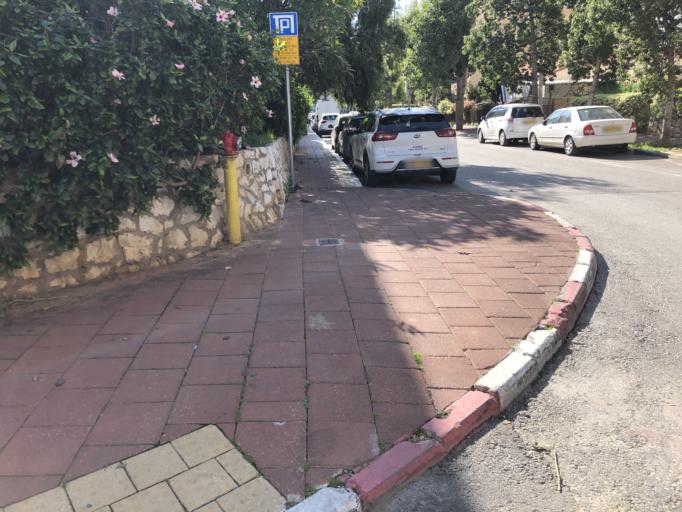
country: IL
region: Tel Aviv
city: Bene Beraq
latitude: 32.0715
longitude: 34.8270
